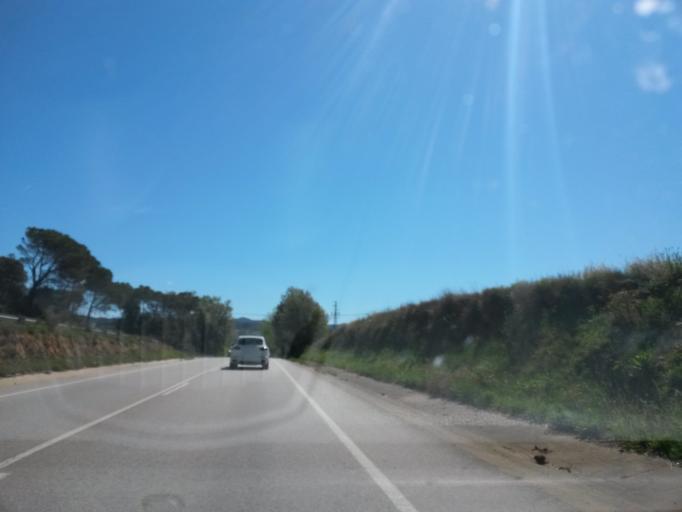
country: ES
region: Catalonia
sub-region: Provincia de Girona
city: Llambilles
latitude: 41.8950
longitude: 2.8451
